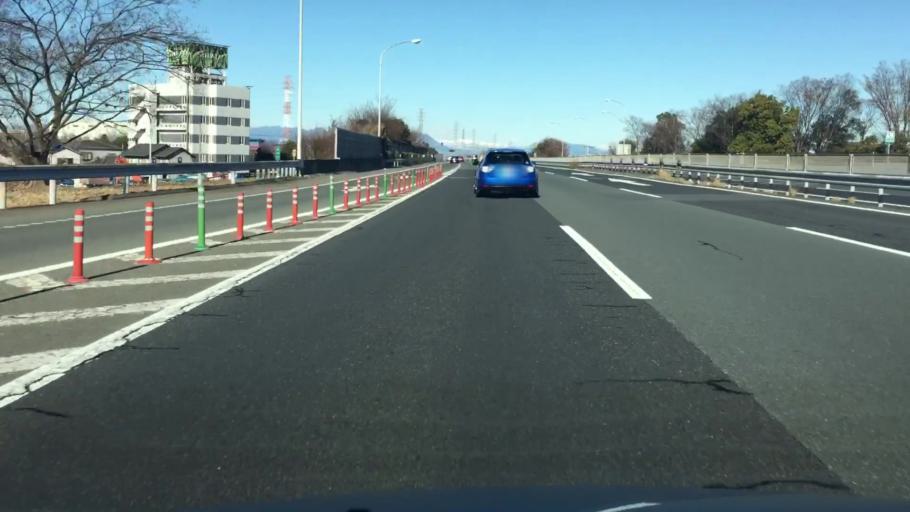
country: JP
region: Saitama
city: Honjo
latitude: 36.2186
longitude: 139.1644
